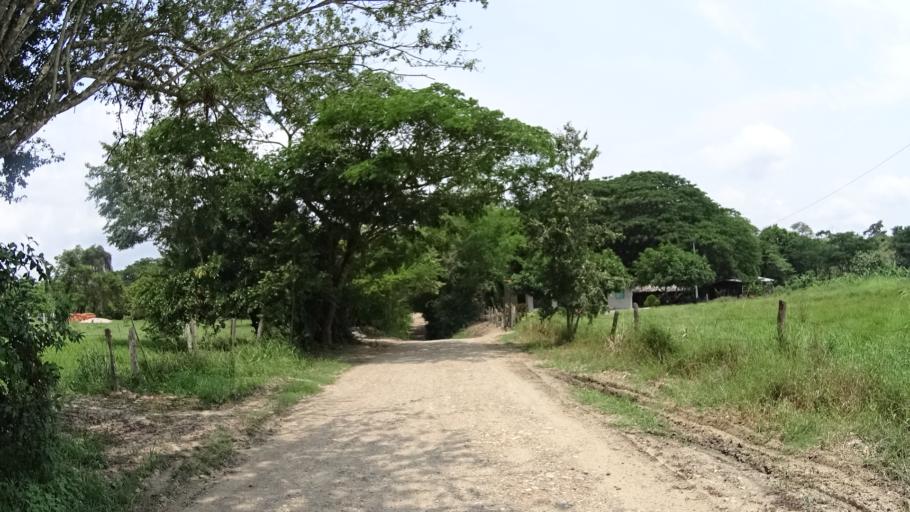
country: CO
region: Cundinamarca
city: Puerto Salgar
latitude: 5.5366
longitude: -74.6829
